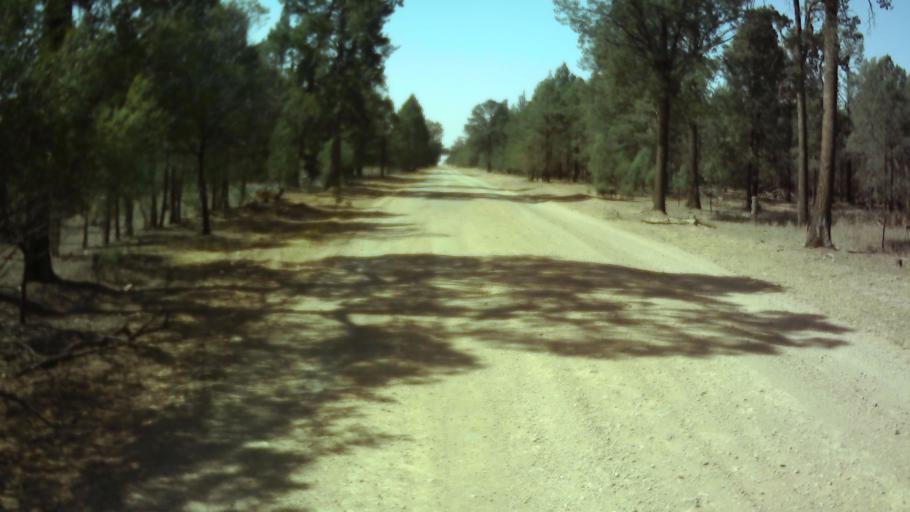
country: AU
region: New South Wales
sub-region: Weddin
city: Grenfell
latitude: -33.9648
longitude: 147.9315
